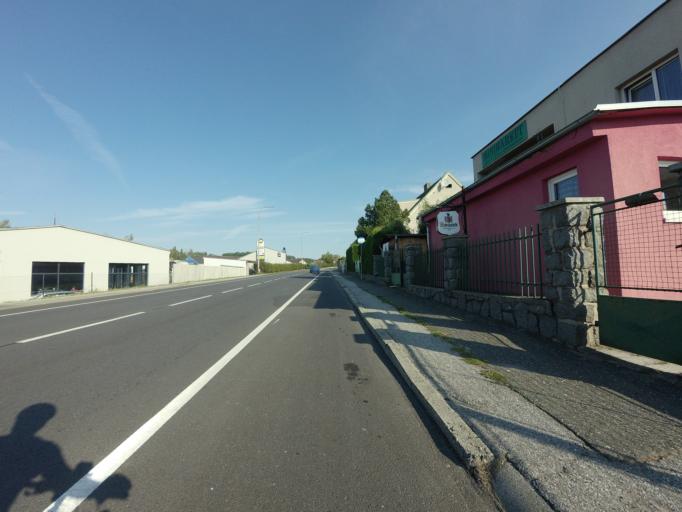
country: CZ
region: Jihocesky
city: Tyn nad Vltavou
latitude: 49.2294
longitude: 14.4224
